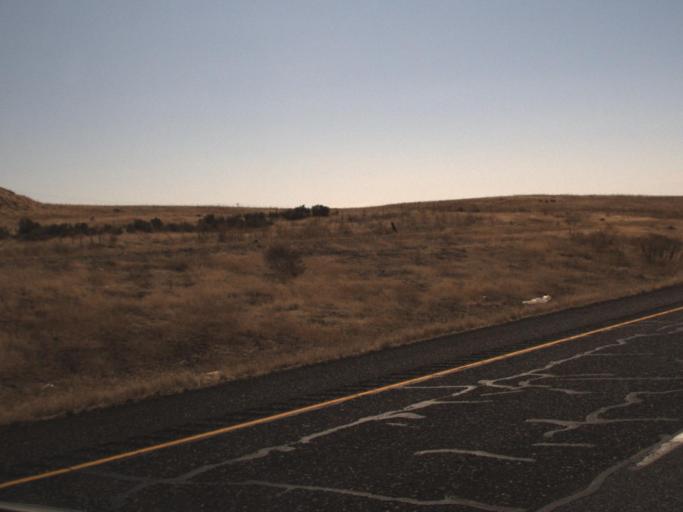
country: US
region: Washington
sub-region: Franklin County
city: Basin City
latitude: 46.5004
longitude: -119.0153
